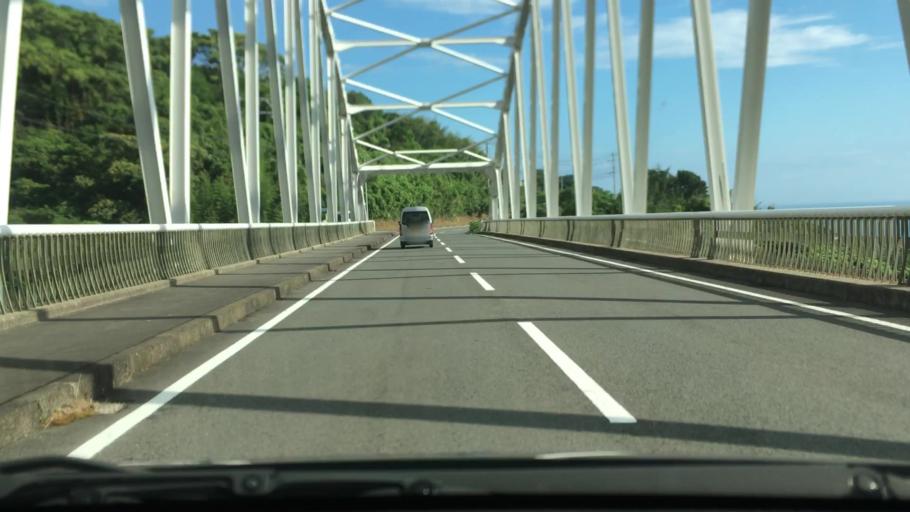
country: JP
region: Nagasaki
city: Togitsu
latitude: 32.8574
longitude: 129.6860
